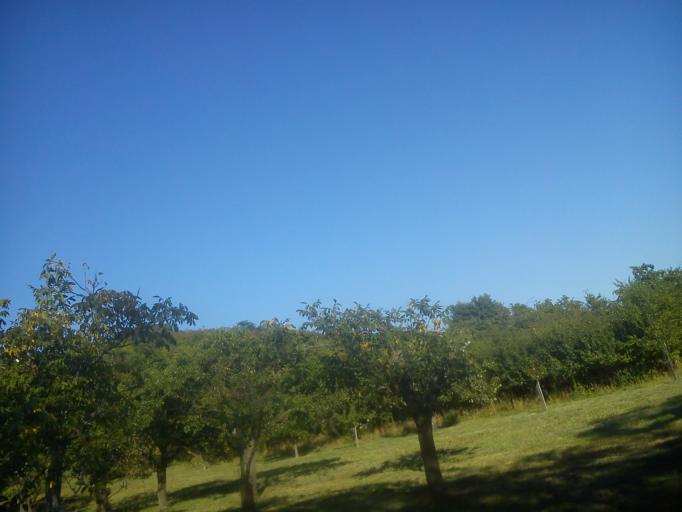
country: CZ
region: South Moravian
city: Sokolnice
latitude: 49.1126
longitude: 16.7651
